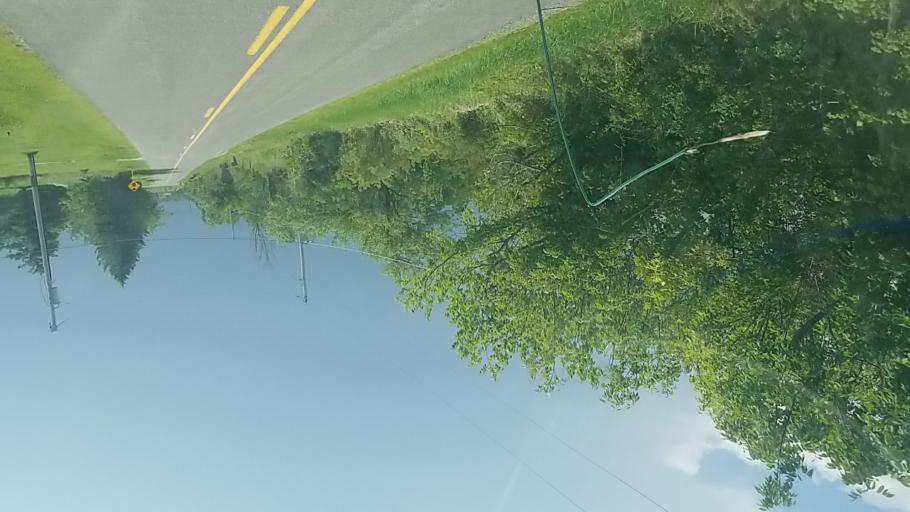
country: US
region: Ohio
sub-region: Medina County
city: Westfield Center
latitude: 41.0923
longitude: -81.9623
